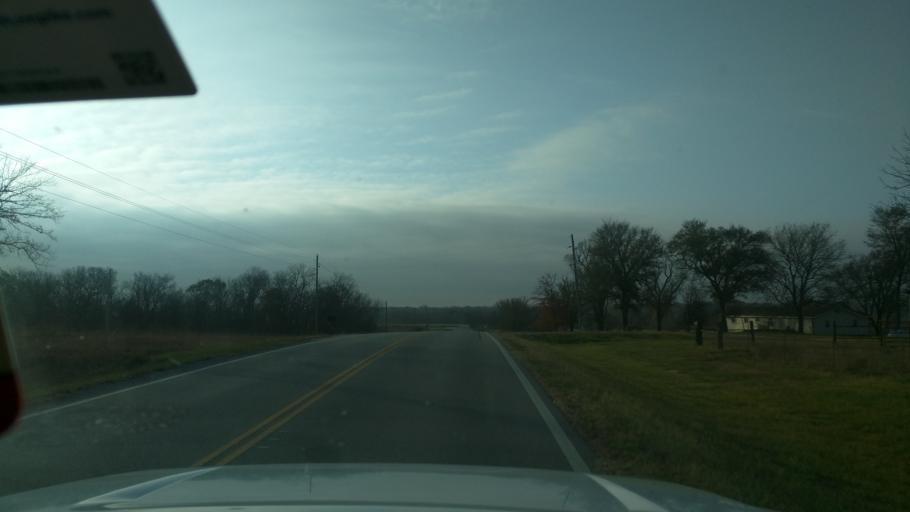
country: US
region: Kansas
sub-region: Greenwood County
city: Eureka
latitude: 37.7550
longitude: -96.2344
